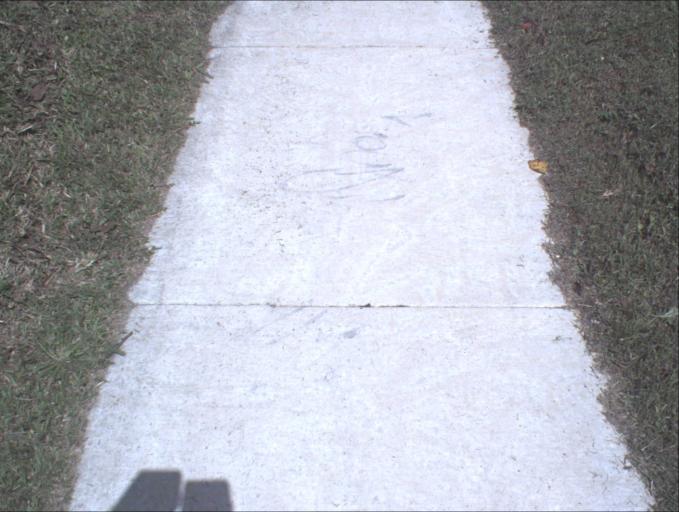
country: AU
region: Queensland
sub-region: Logan
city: Park Ridge South
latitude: -27.6740
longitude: 153.0239
